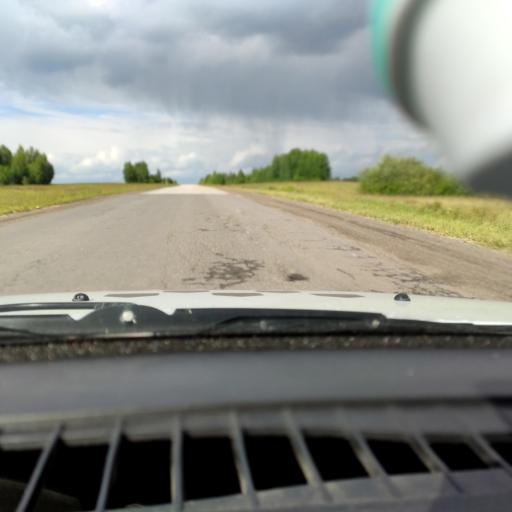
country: RU
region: Perm
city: Orda
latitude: 57.1838
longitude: 56.8438
